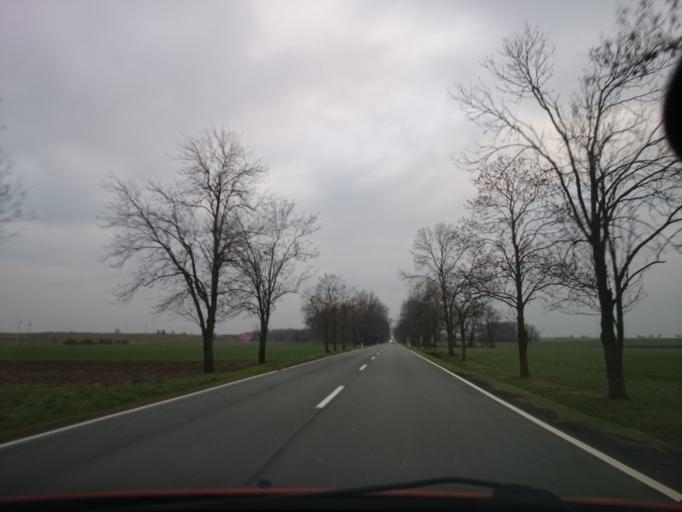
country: PL
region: Opole Voivodeship
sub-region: Powiat nyski
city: Pakoslawice
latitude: 50.5240
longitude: 17.3584
